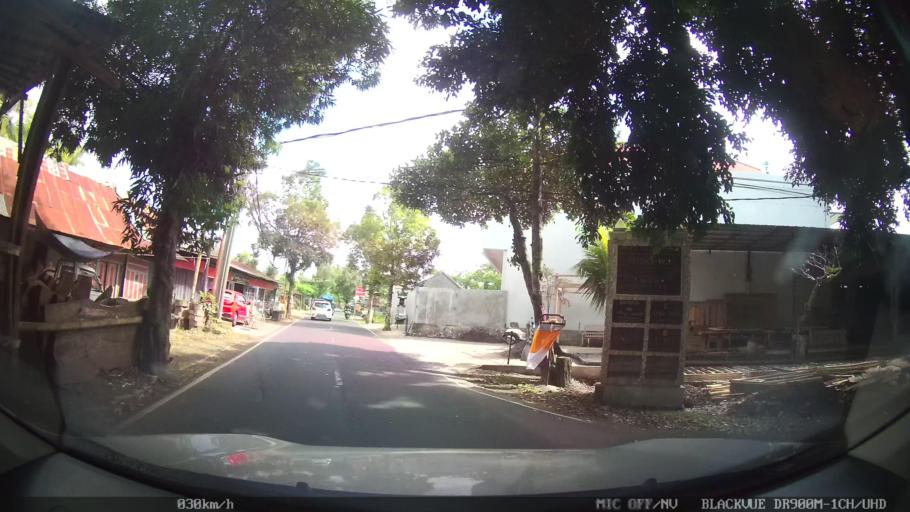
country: ID
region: Bali
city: Banjar Tebongkang
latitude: -8.5443
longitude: 115.2493
